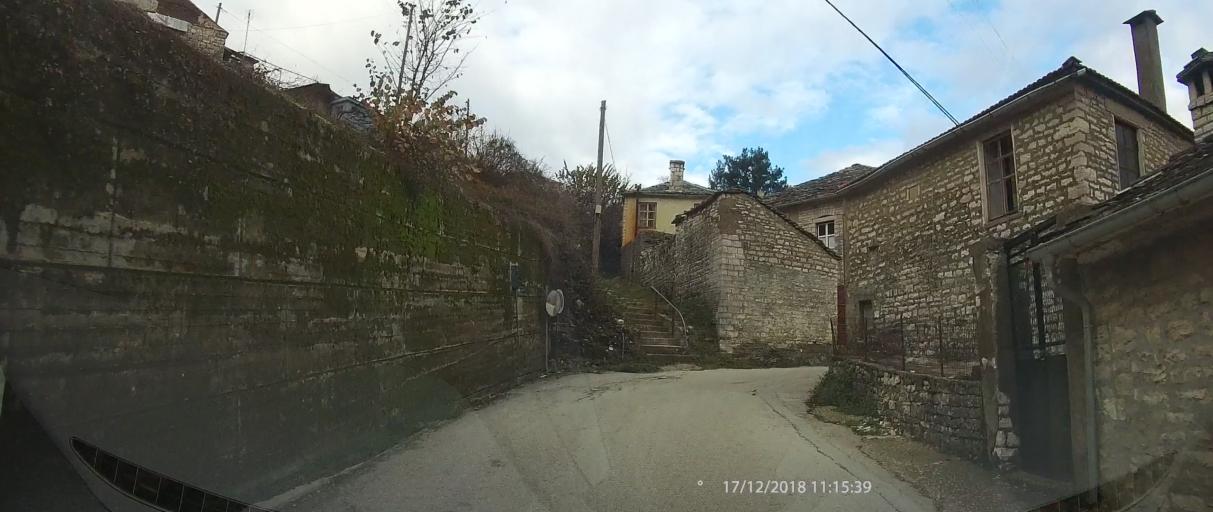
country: GR
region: Epirus
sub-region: Nomos Ioanninon
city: Kalpaki
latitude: 39.9347
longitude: 20.6713
